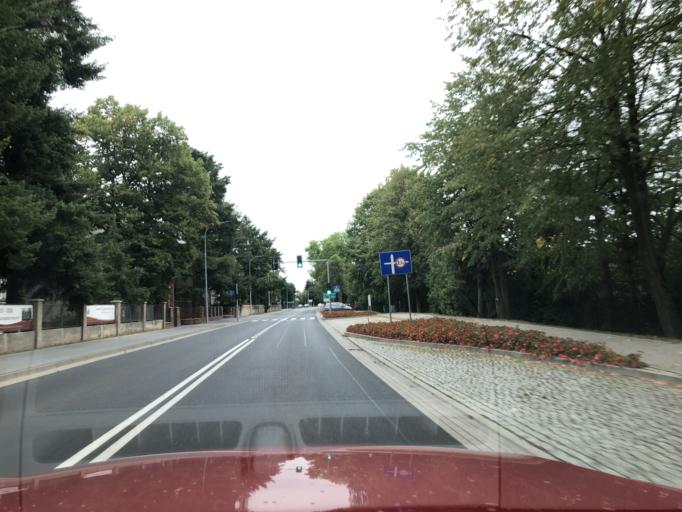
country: PL
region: Greater Poland Voivodeship
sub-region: Powiat szamotulski
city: Pniewy
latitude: 52.5164
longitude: 16.2455
